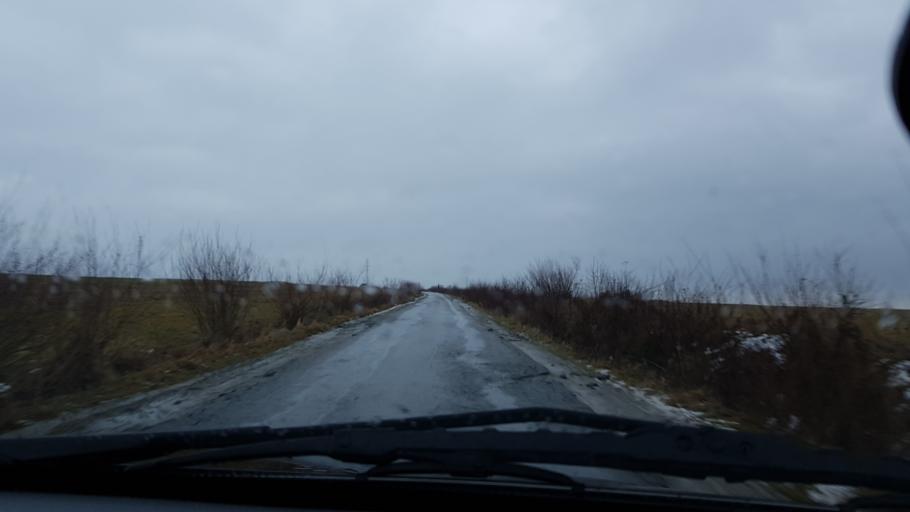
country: PL
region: Lesser Poland Voivodeship
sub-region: Powiat nowotarski
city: Sieniawa
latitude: 49.4879
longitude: 19.9208
